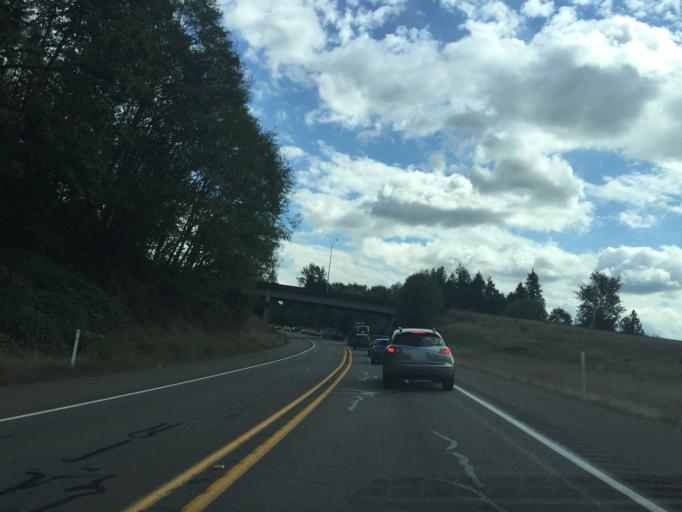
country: US
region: Washington
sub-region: Snohomish County
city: Snohomish
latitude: 47.9166
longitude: -122.0732
